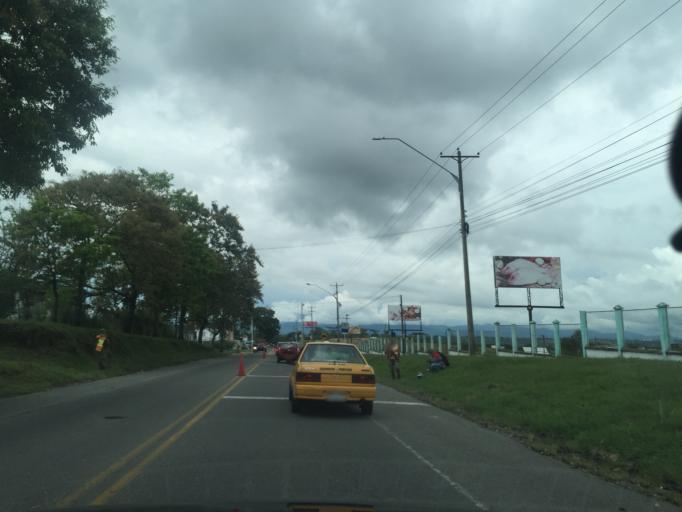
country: CO
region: Quindio
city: Armenia
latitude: 4.5275
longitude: -75.7144
